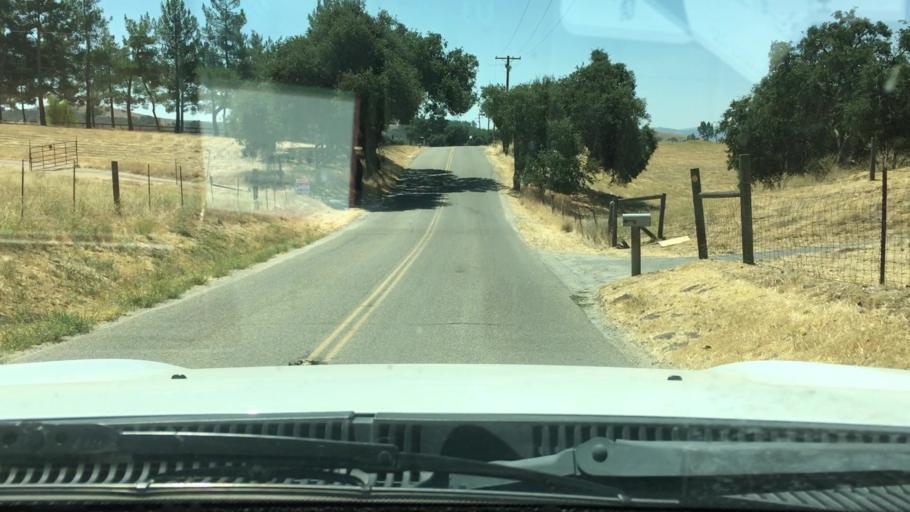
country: US
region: California
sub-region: San Luis Obispo County
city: Atascadero
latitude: 35.5179
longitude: -120.6403
